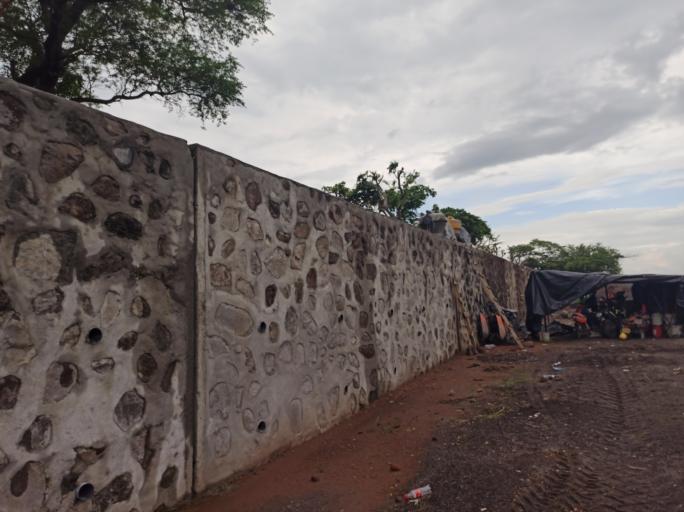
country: NI
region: Granada
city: Granada
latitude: 11.9476
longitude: -85.9456
